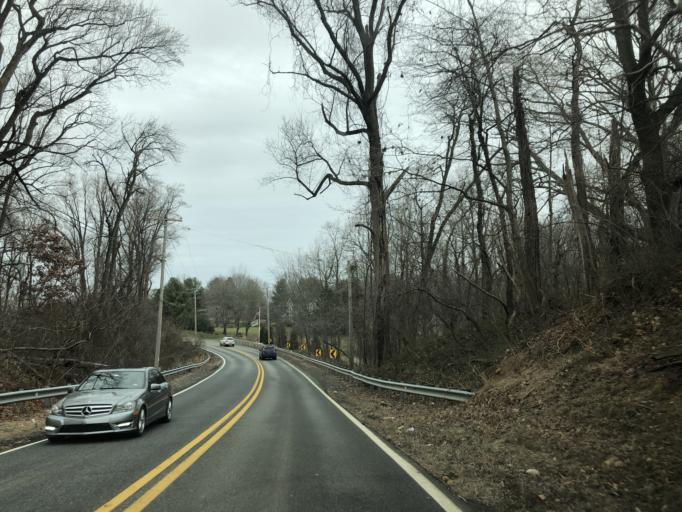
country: US
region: Delaware
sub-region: New Castle County
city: Middletown
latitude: 39.4918
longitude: -75.6905
